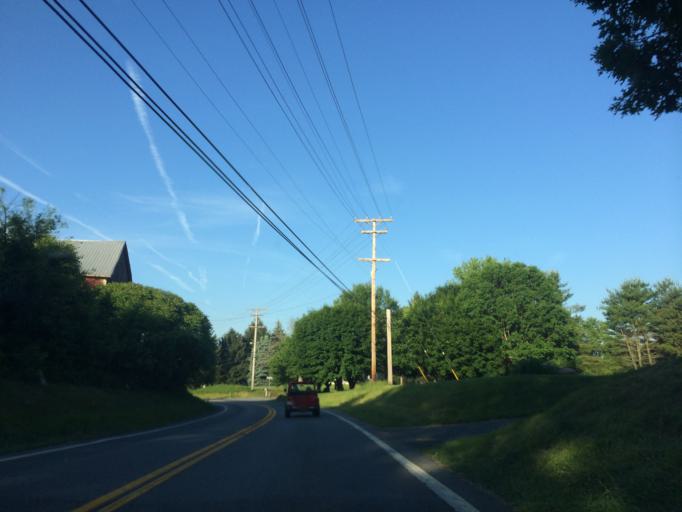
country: US
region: Maryland
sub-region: Carroll County
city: Sykesville
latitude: 39.3690
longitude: -77.0172
